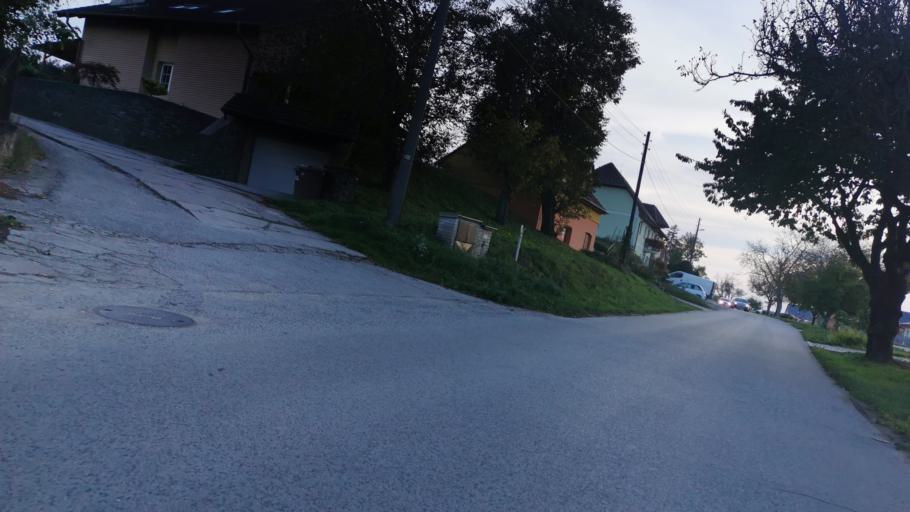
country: SK
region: Trnavsky
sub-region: Okres Skalica
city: Skalica
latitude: 48.8337
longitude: 17.2284
